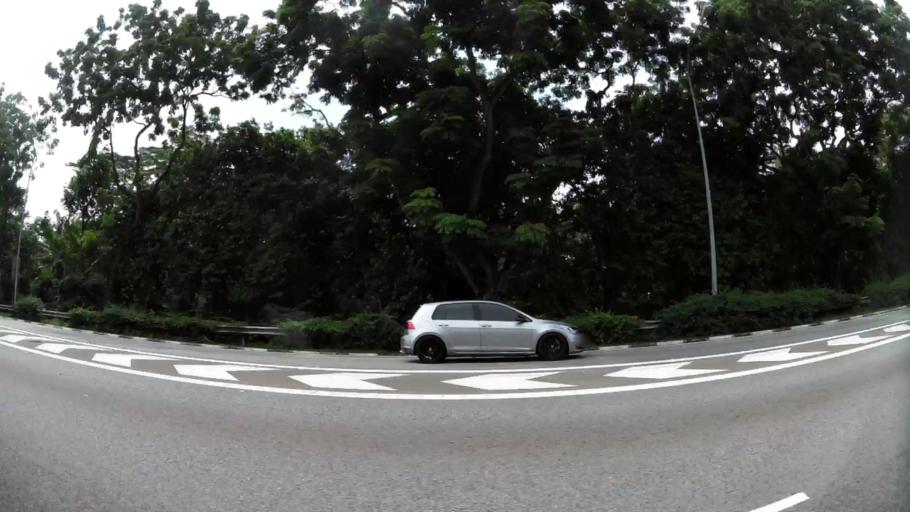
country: SG
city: Singapore
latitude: 1.3685
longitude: 103.9436
